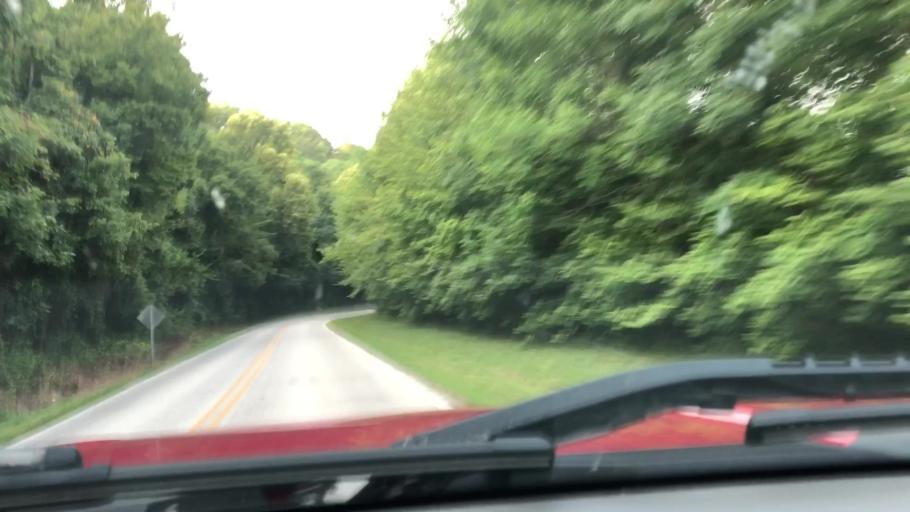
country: US
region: Missouri
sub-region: Jasper County
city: Duquesne
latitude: 37.0157
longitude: -94.4920
